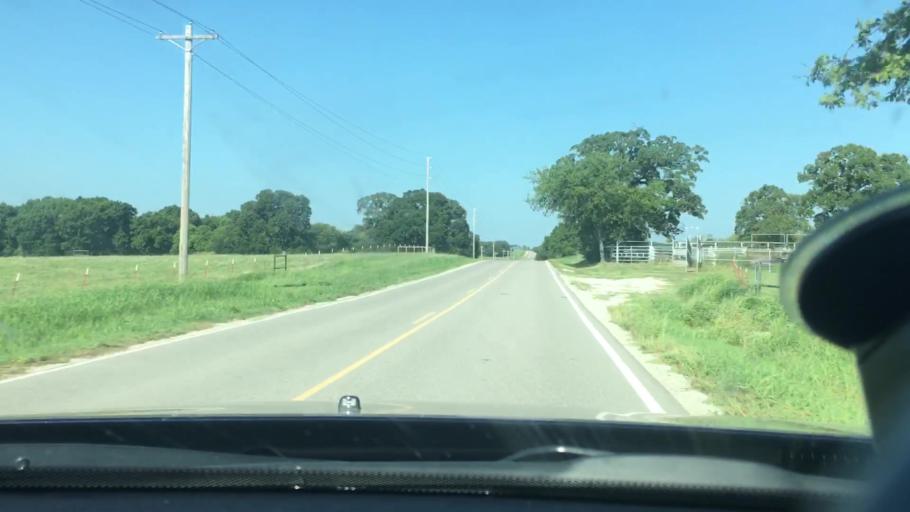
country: US
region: Oklahoma
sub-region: Love County
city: Marietta
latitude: 34.0275
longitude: -97.1854
